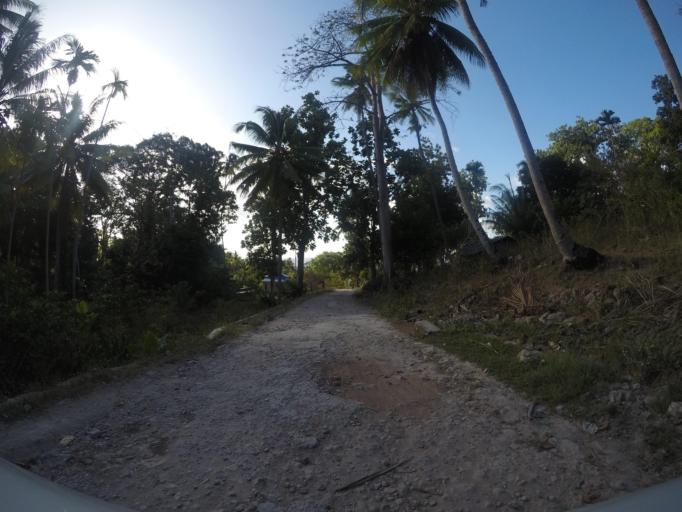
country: TL
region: Lautem
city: Lospalos
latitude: -8.4384
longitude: 126.8541
